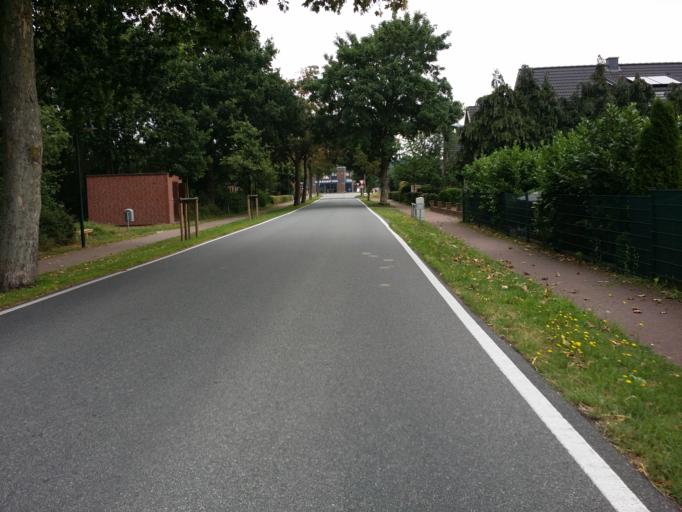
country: DE
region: Schleswig-Holstein
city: Krempermoor
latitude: 53.8794
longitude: 9.4775
